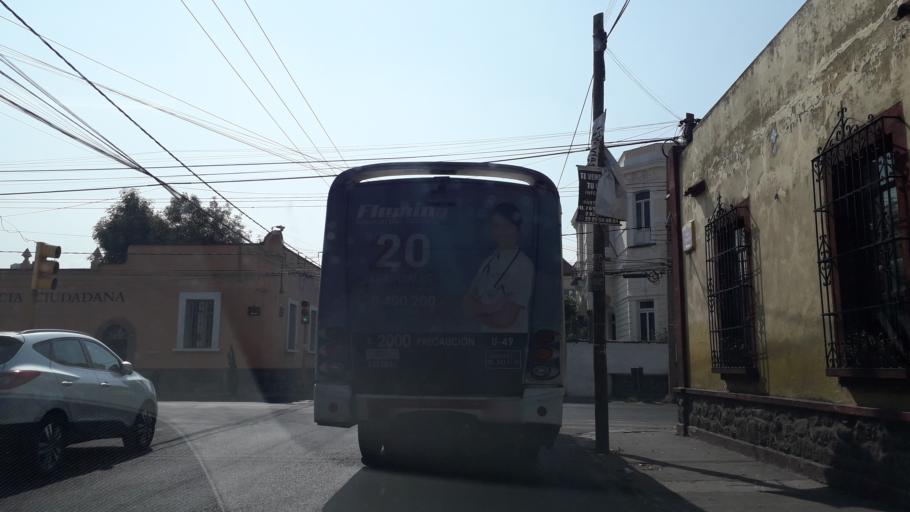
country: MX
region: Puebla
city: Puebla
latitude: 19.0414
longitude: -98.2120
